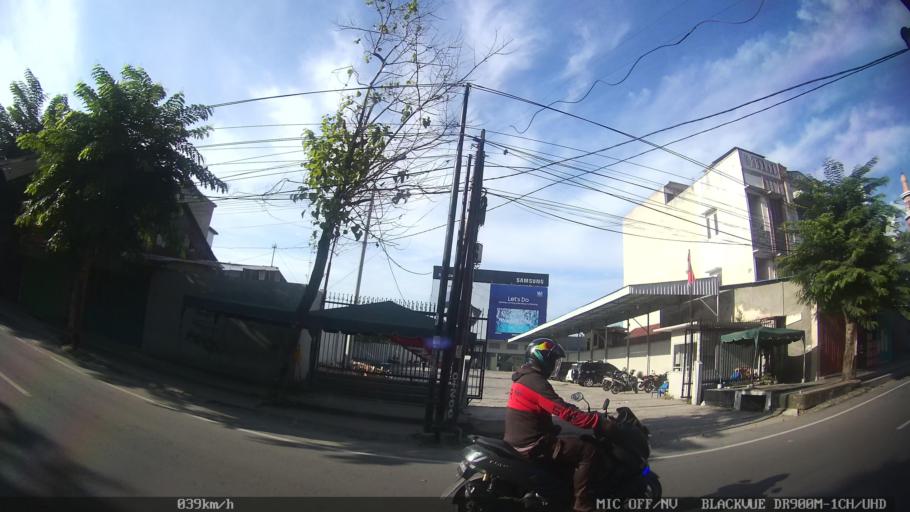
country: ID
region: North Sumatra
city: Medan
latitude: 3.5903
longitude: 98.6477
